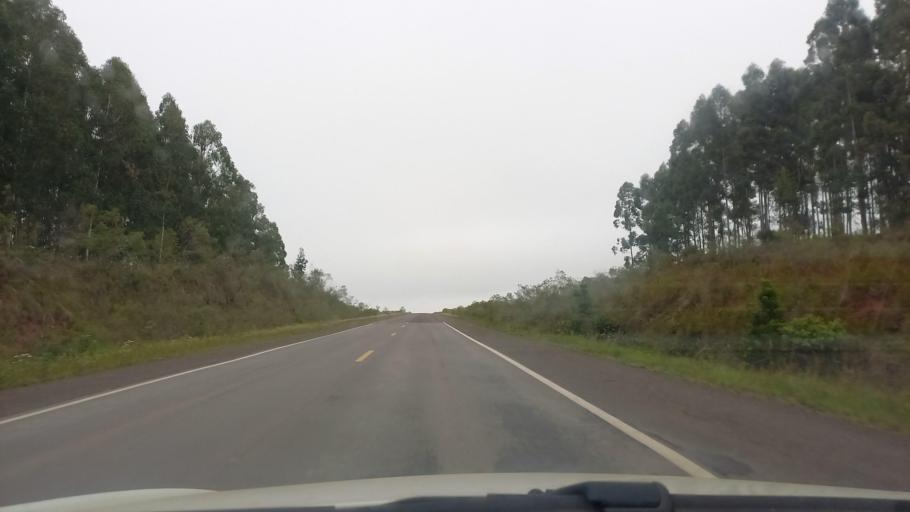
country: BR
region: Rio Grande do Sul
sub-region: Cacequi
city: Cacequi
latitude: -30.0437
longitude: -54.5948
